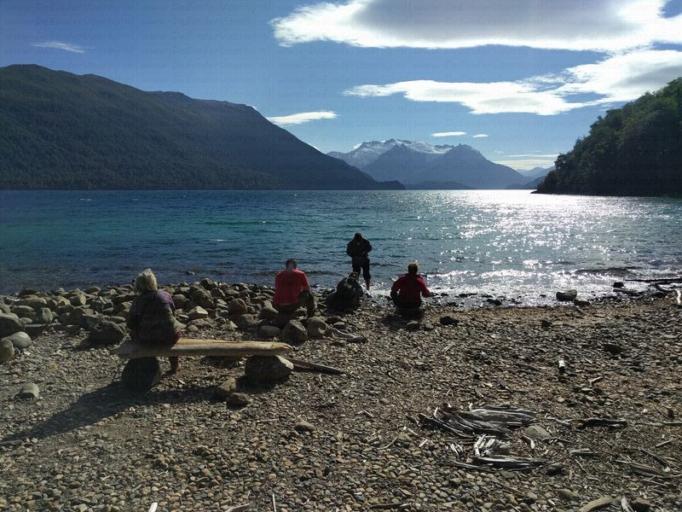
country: AR
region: Chubut
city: Trevelin
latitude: -42.7288
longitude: -71.7588
